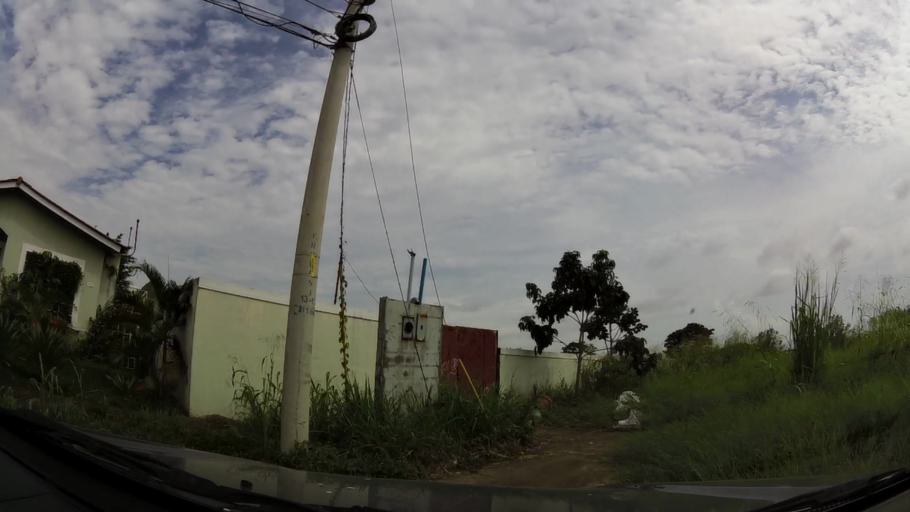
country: PA
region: Panama
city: Tocumen
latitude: 9.0400
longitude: -79.4099
